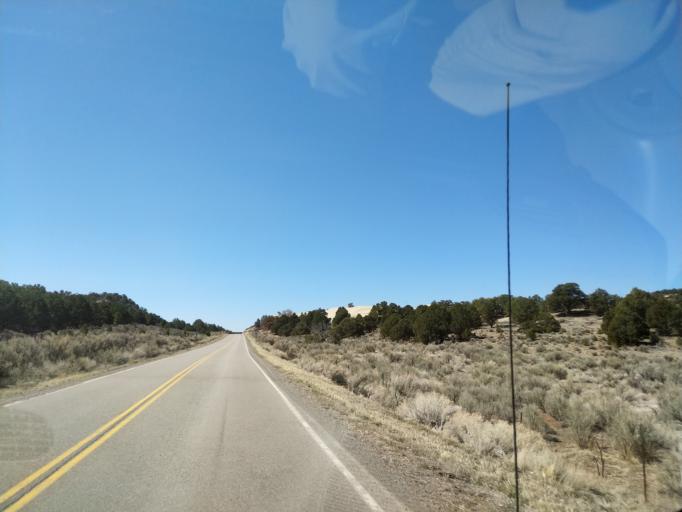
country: US
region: Colorado
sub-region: Mesa County
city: Redlands
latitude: 38.9888
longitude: -108.7869
